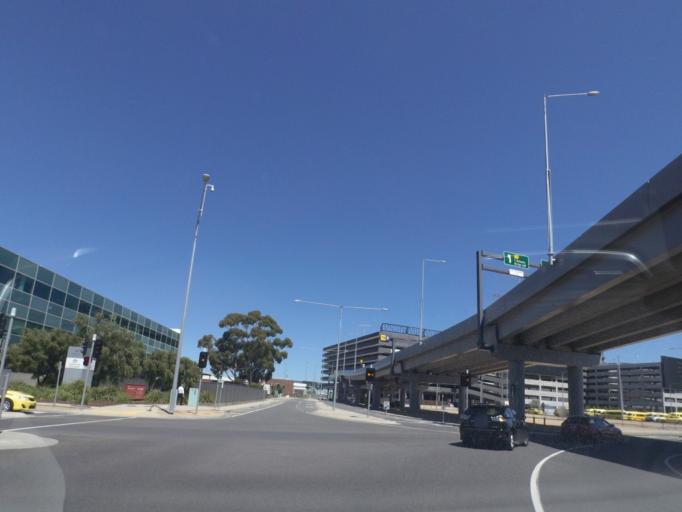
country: AU
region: Victoria
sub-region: Hume
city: Westmeadows
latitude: -37.6756
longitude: 144.8524
